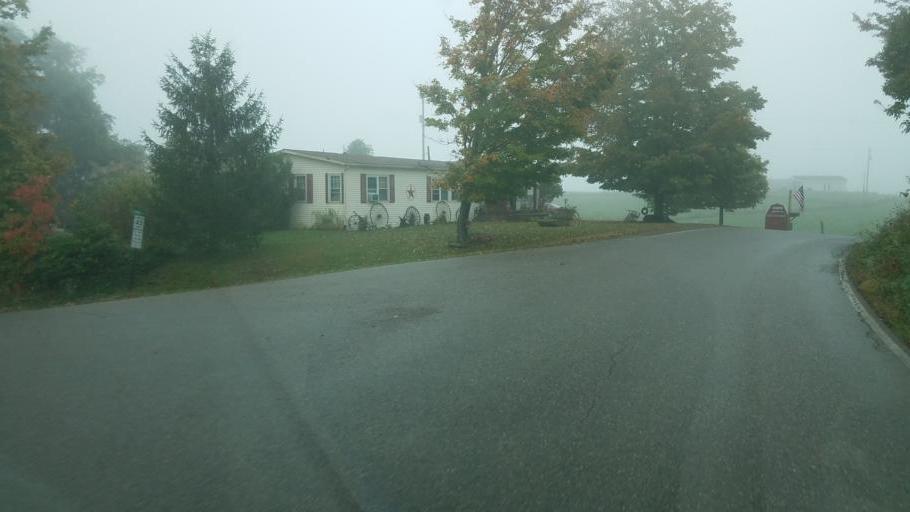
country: US
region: Ohio
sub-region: Harrison County
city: Cadiz
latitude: 40.3858
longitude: -81.1124
